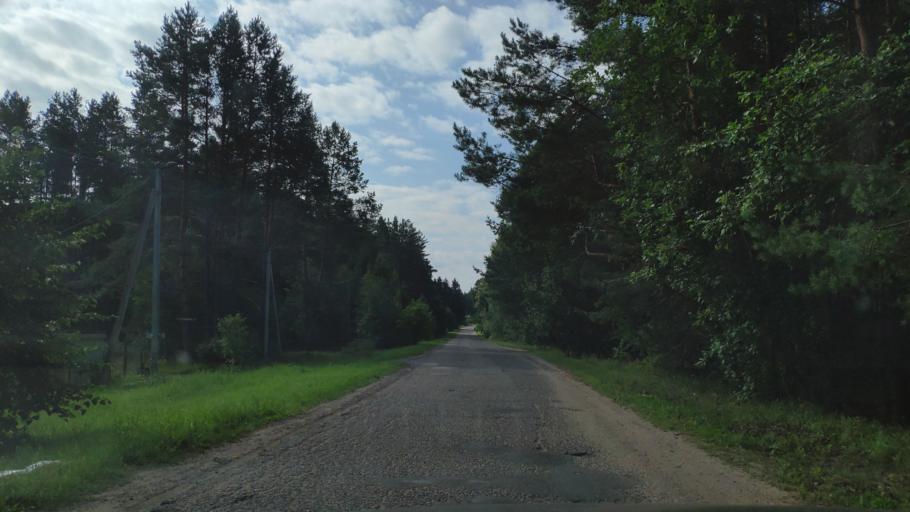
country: BY
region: Minsk
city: Zaslawye
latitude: 53.9809
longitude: 27.2893
